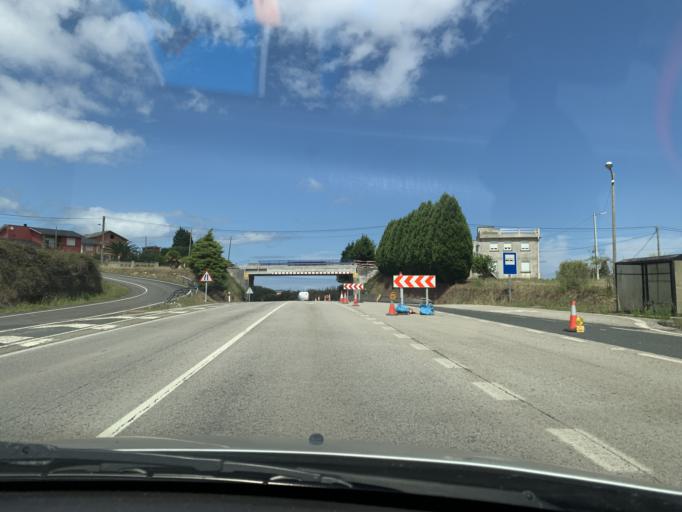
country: ES
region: Galicia
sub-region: Provincia de Lugo
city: Foz
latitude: 43.5515
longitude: -7.2666
